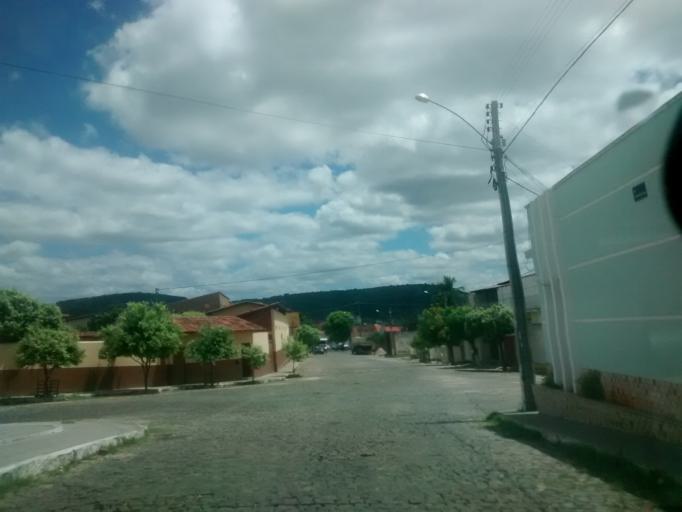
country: BR
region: Bahia
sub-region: Brumado
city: Brumado
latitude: -14.2012
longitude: -41.6694
